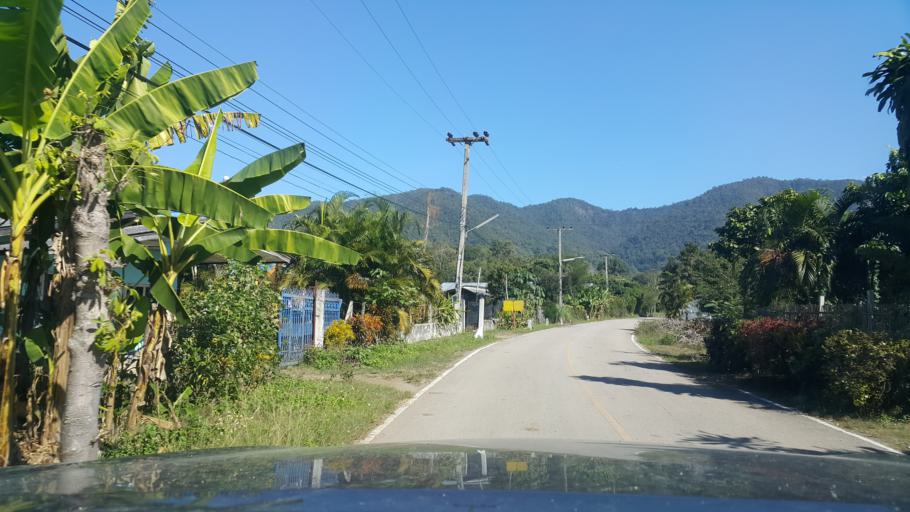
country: TH
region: Chiang Mai
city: Mae On
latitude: 18.7834
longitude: 99.2616
